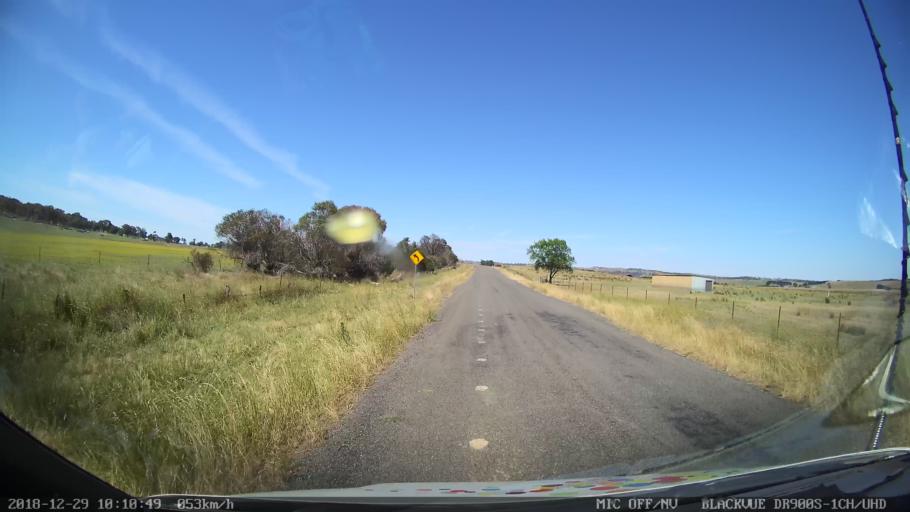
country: AU
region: New South Wales
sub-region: Yass Valley
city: Gundaroo
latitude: -34.8786
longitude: 149.4554
